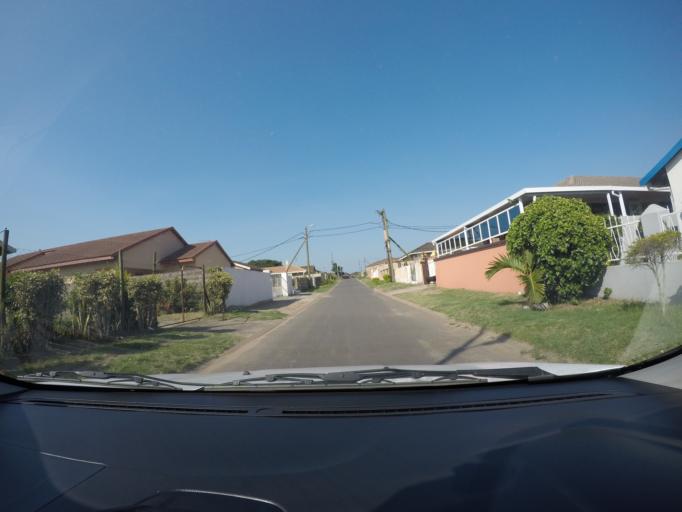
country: ZA
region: KwaZulu-Natal
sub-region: uThungulu District Municipality
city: Richards Bay
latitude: -28.7217
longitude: 32.0383
